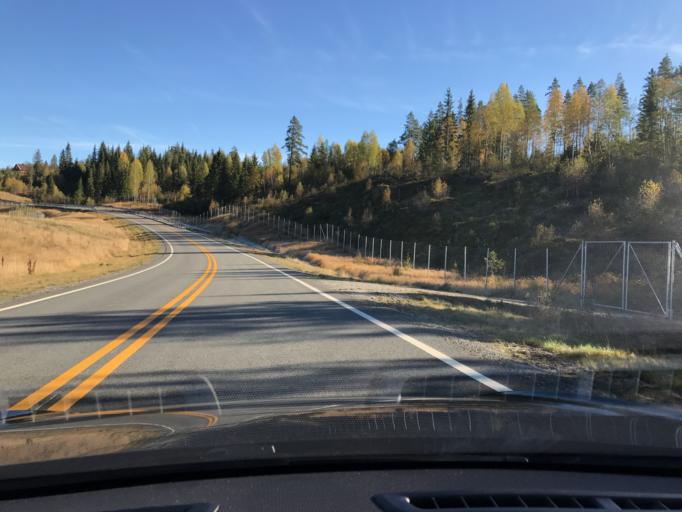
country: NO
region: Buskerud
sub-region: Krodsherad
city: Noresund
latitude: 60.2660
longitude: 9.7912
